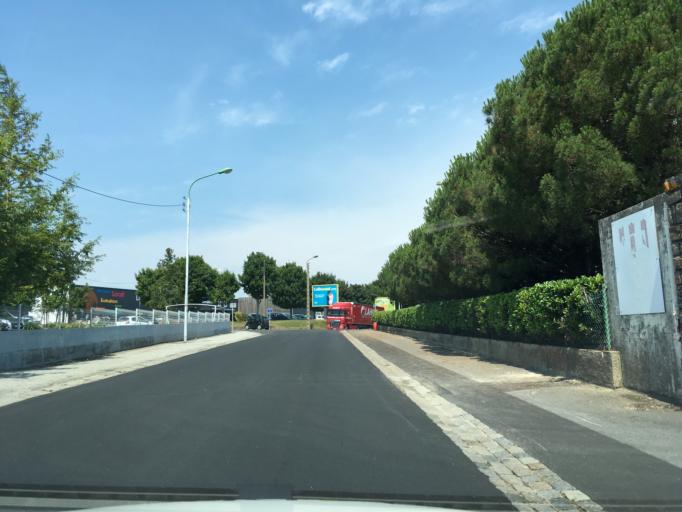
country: FR
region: Brittany
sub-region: Departement du Morbihan
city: Queven
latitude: 47.7646
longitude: -3.4021
